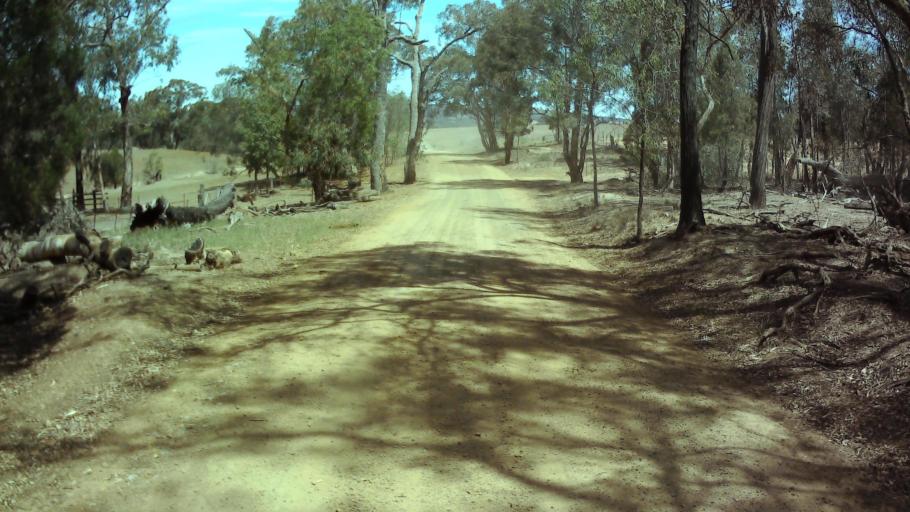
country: AU
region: New South Wales
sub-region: Weddin
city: Grenfell
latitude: -33.8198
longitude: 148.1672
